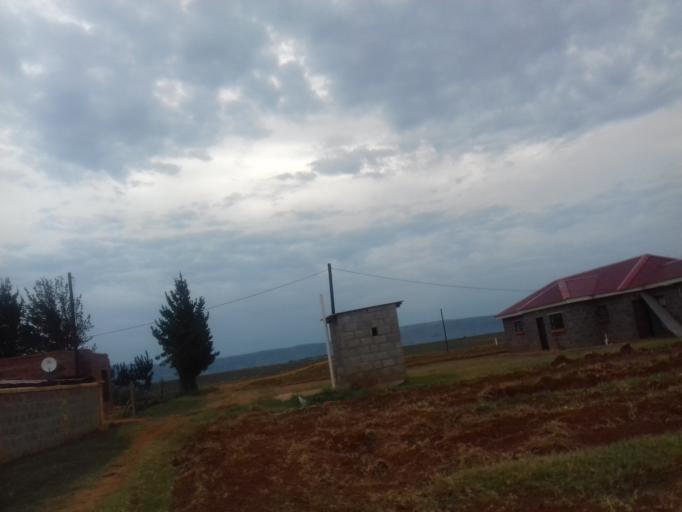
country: LS
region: Maseru
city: Maseru
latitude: -29.4247
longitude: 27.5681
